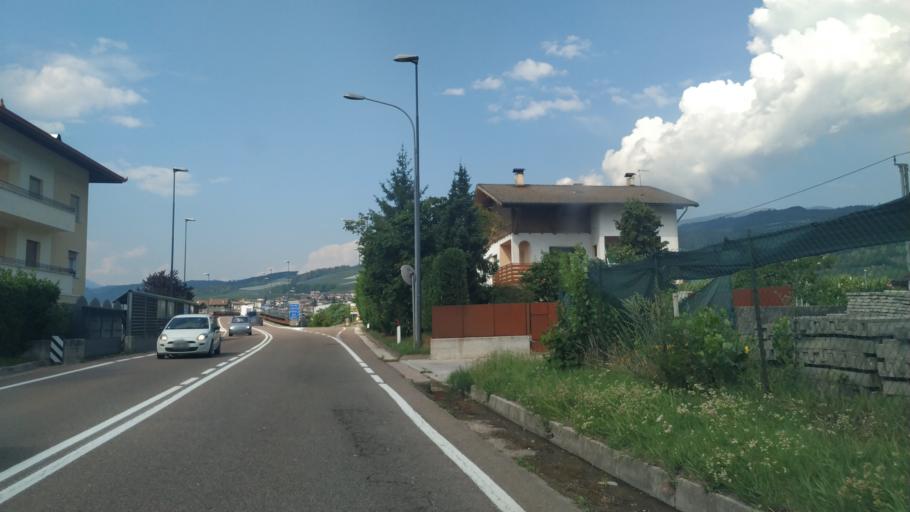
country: IT
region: Trentino-Alto Adige
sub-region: Provincia di Trento
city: Taio
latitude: 46.2951
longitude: 11.0678
